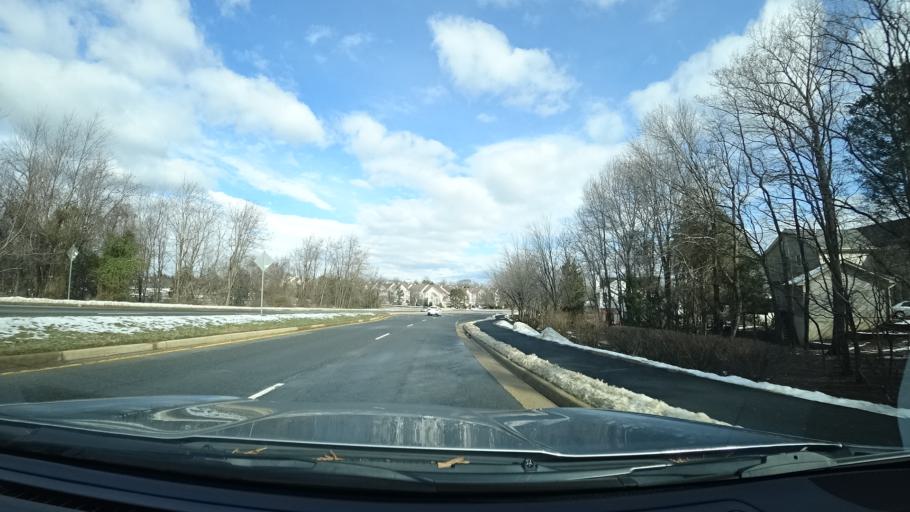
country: US
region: Virginia
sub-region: Loudoun County
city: Sugarland Run
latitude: 39.0431
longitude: -77.3840
